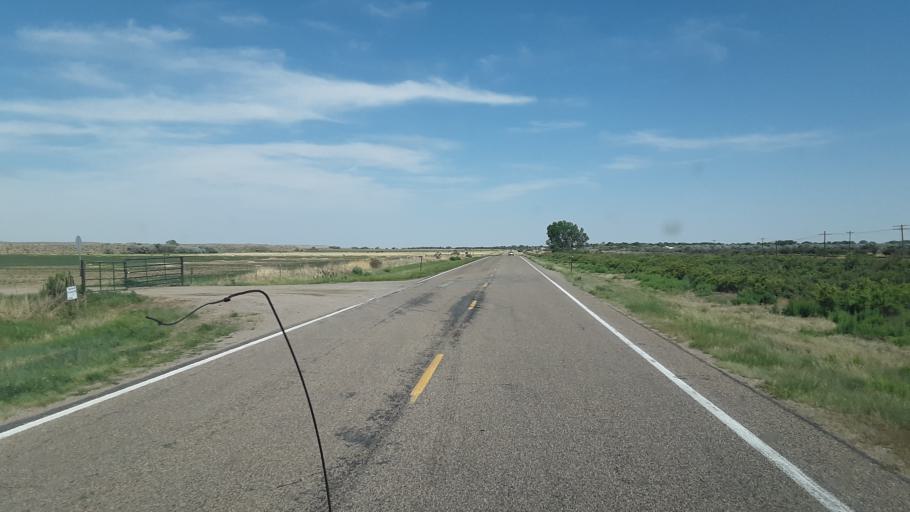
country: US
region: Colorado
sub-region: Otero County
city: Fowler
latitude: 38.2013
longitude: -104.1685
